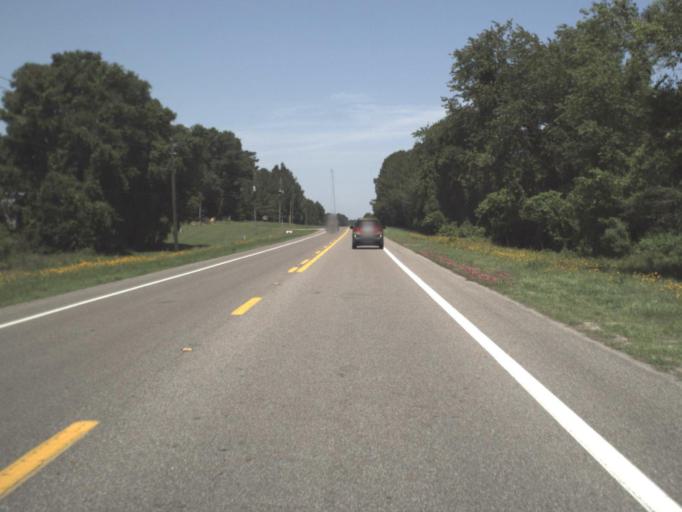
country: US
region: Florida
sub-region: Suwannee County
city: Live Oak
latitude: 30.2675
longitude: -82.9222
